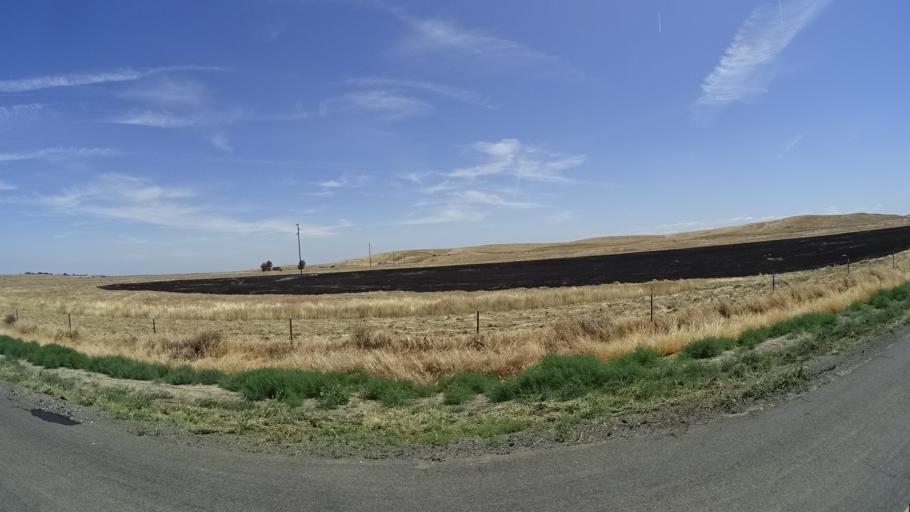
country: US
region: California
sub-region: Kings County
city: Kettleman City
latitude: 35.8426
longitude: -119.9153
